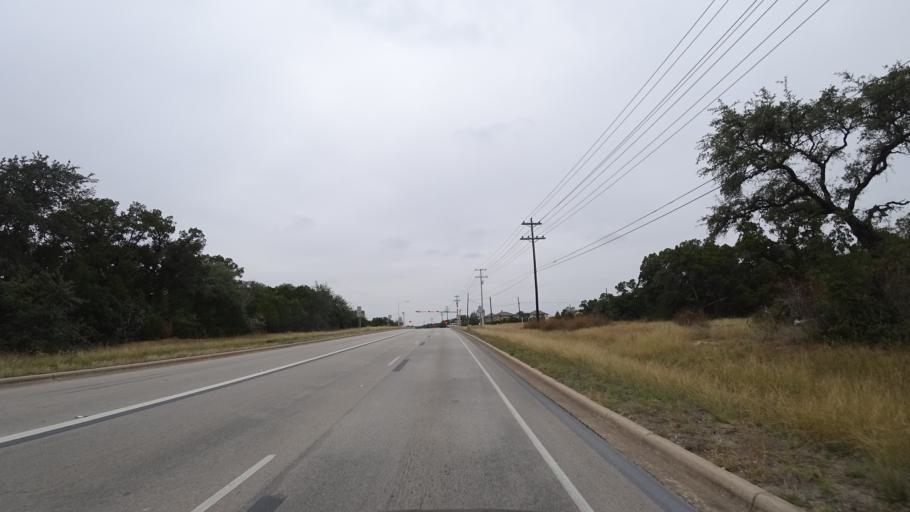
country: US
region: Texas
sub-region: Travis County
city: Shady Hollow
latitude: 30.1815
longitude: -97.8984
